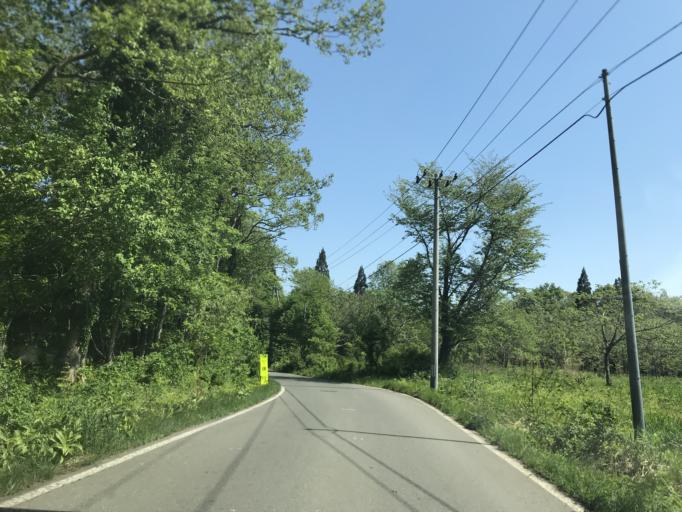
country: JP
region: Iwate
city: Shizukuishi
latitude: 39.5617
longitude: 140.8396
